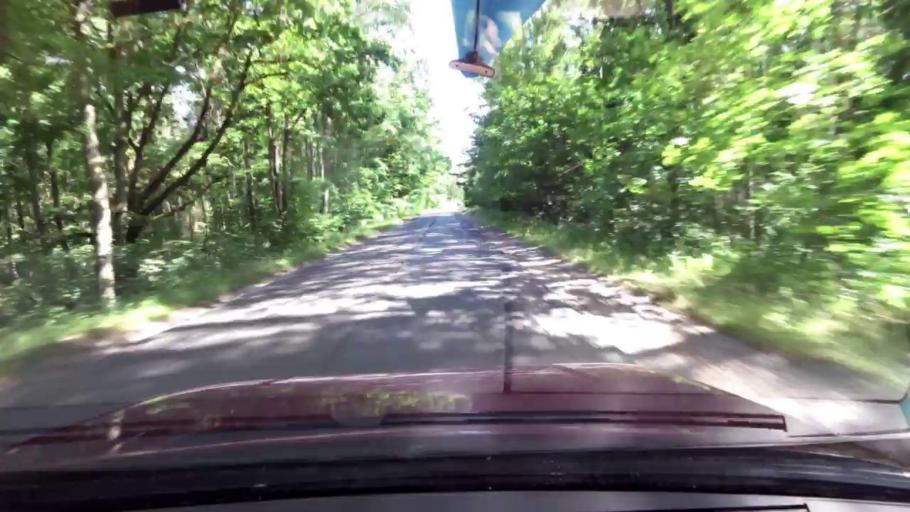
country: PL
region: Pomeranian Voivodeship
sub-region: Powiat slupski
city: Kepice
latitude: 54.3311
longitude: 16.9605
